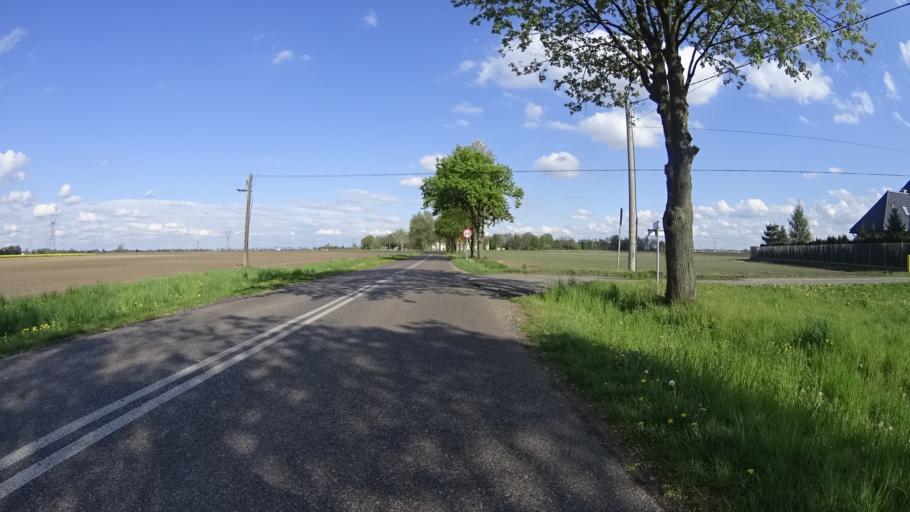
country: PL
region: Masovian Voivodeship
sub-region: Powiat warszawski zachodni
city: Jozefow
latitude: 52.2328
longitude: 20.6852
